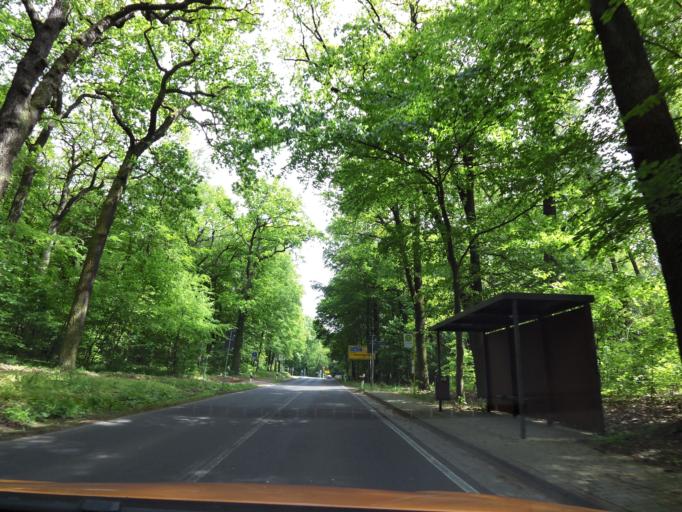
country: DE
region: Brandenburg
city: Michendorf
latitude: 52.2792
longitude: 13.0055
